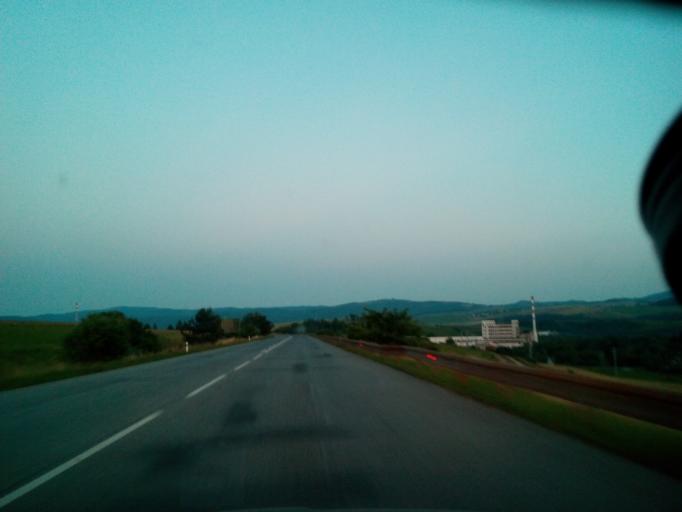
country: SK
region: Kosicky
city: Spisska Nova Ves
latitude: 48.9426
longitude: 20.5847
